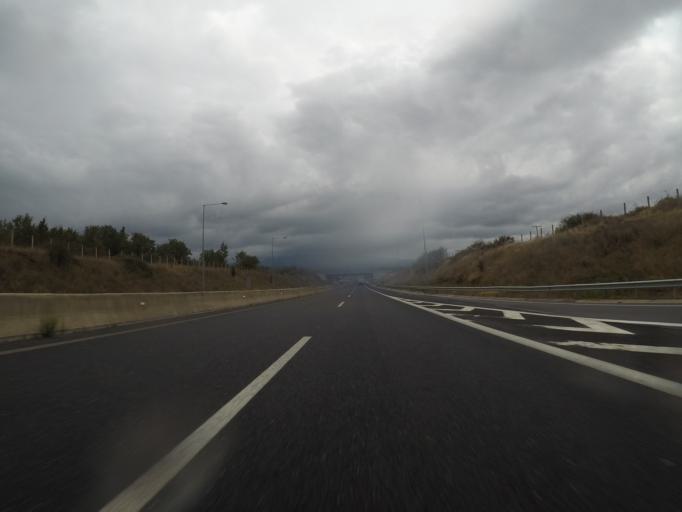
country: GR
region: Peloponnese
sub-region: Nomos Arkadias
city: Megalopoli
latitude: 37.3813
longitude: 22.1646
